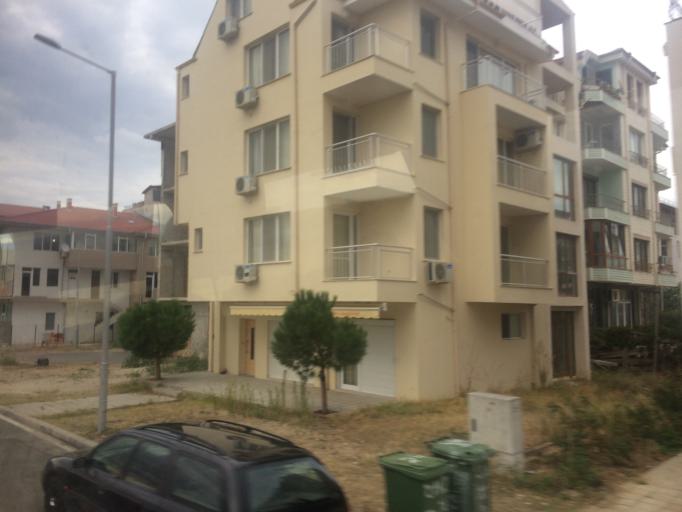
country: BG
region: Burgas
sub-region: Obshtina Nesebur
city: Ravda
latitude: 42.6572
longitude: 27.7024
